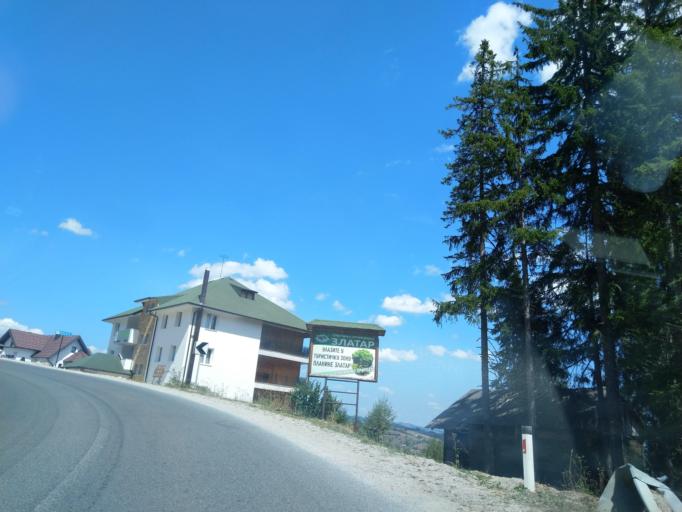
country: RS
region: Central Serbia
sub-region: Zlatiborski Okrug
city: Nova Varos
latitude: 43.4467
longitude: 19.8215
